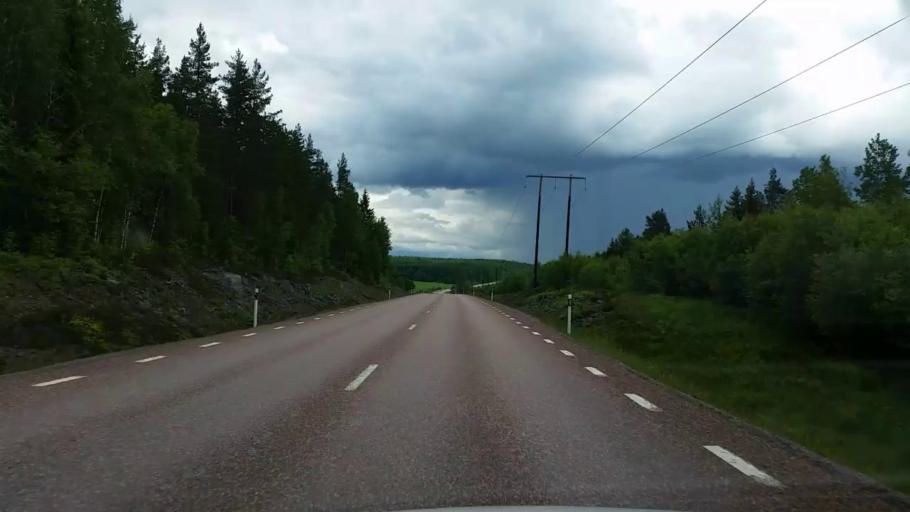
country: SE
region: Gaevleborg
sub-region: Hofors Kommun
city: Hofors
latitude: 60.5322
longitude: 16.4575
